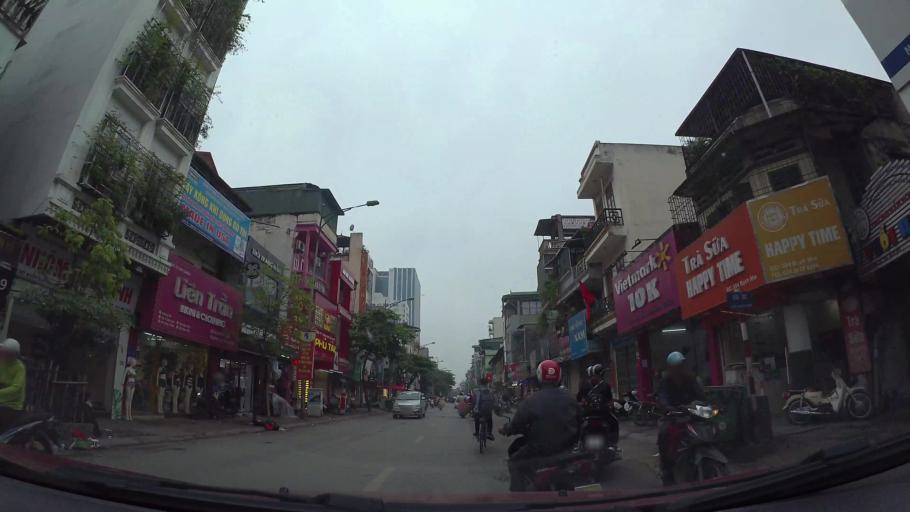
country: VN
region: Ha Noi
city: Hai BaTrung
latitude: 20.9997
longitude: 105.8504
